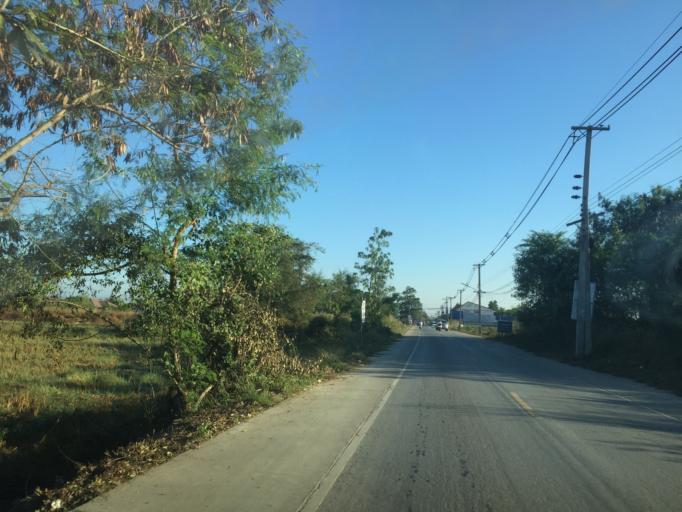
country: TH
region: Lamphun
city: Lamphun
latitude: 18.6023
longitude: 99.0524
